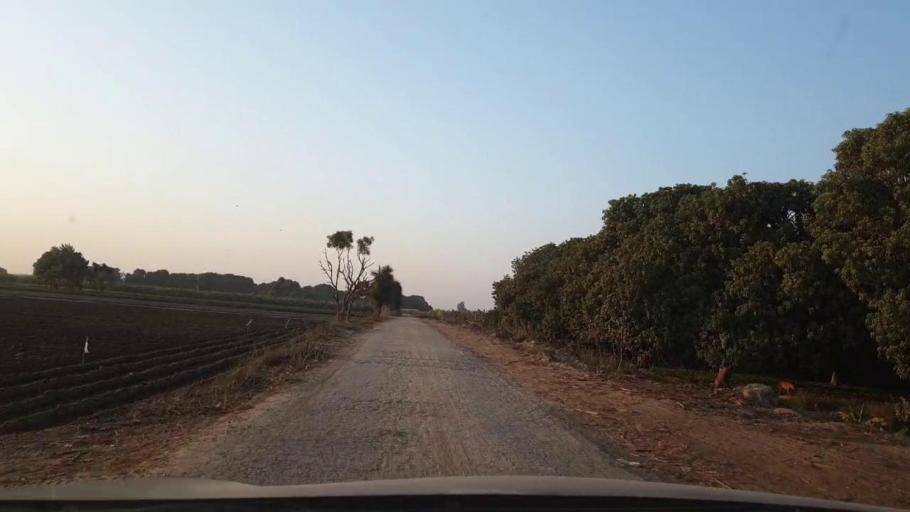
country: PK
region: Sindh
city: Tando Allahyar
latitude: 25.4940
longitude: 68.7429
